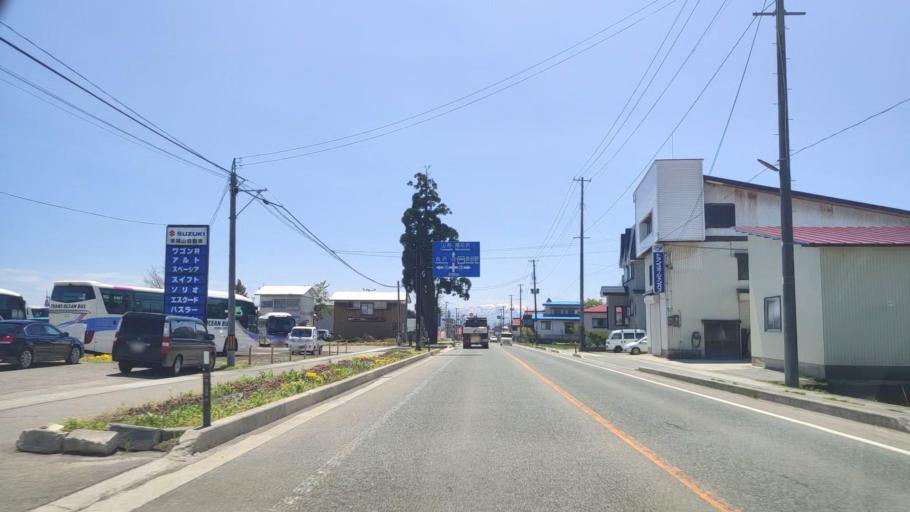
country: JP
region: Yamagata
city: Shinjo
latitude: 38.8147
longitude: 140.3245
